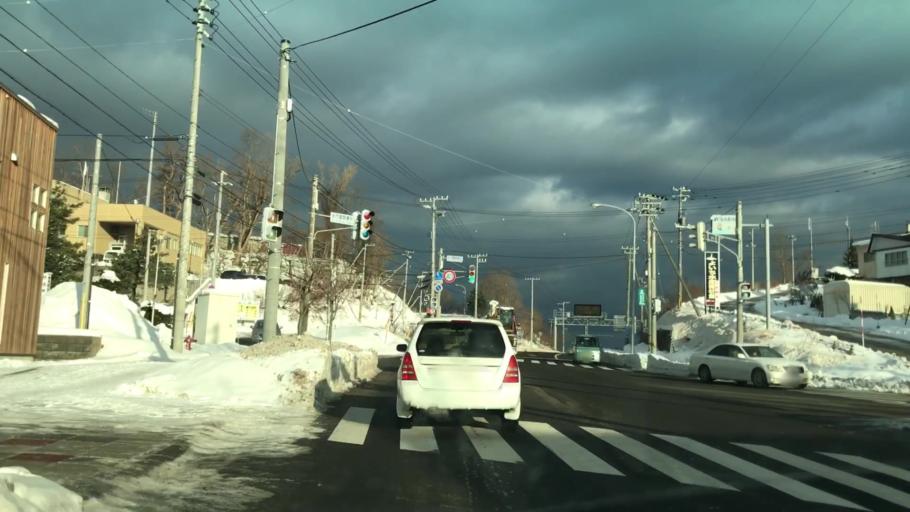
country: JP
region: Hokkaido
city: Yoichi
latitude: 43.1951
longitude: 140.7848
